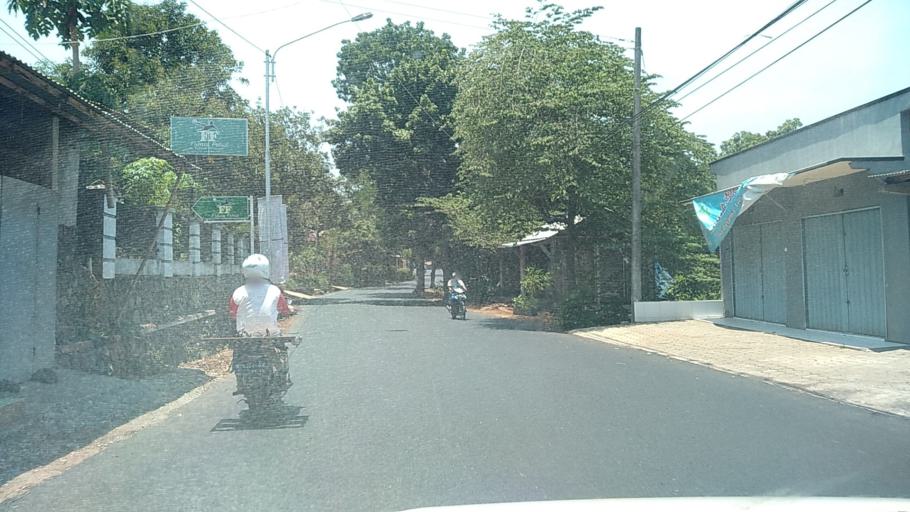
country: ID
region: Central Java
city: Semarang
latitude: -7.0534
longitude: 110.3593
